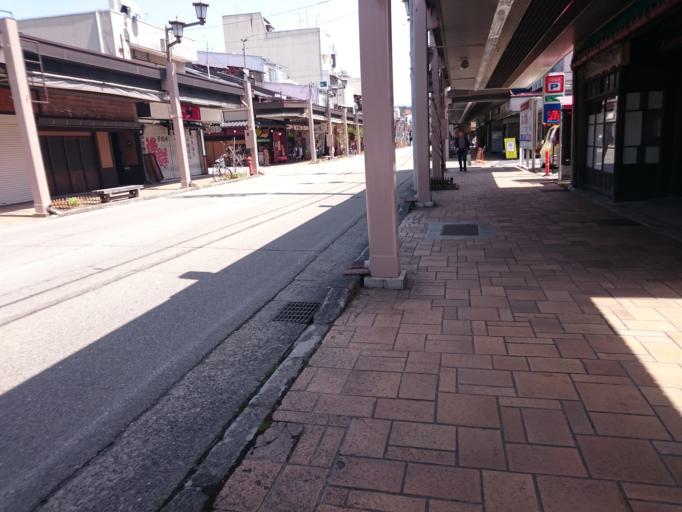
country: JP
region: Gifu
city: Takayama
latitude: 36.1428
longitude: 137.2547
